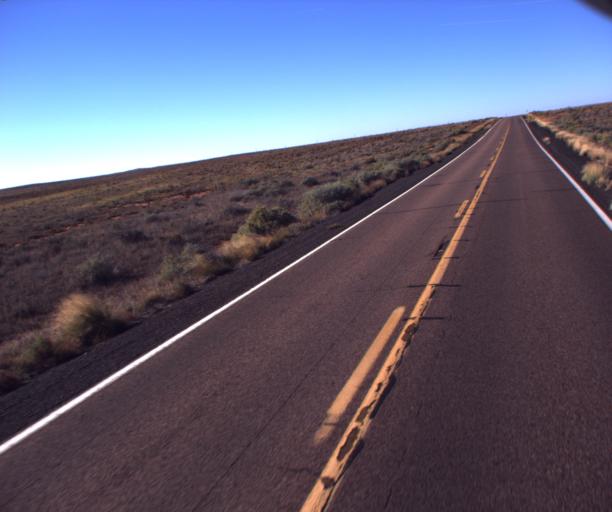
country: US
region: Arizona
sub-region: Navajo County
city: Holbrook
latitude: 34.8277
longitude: -110.1904
